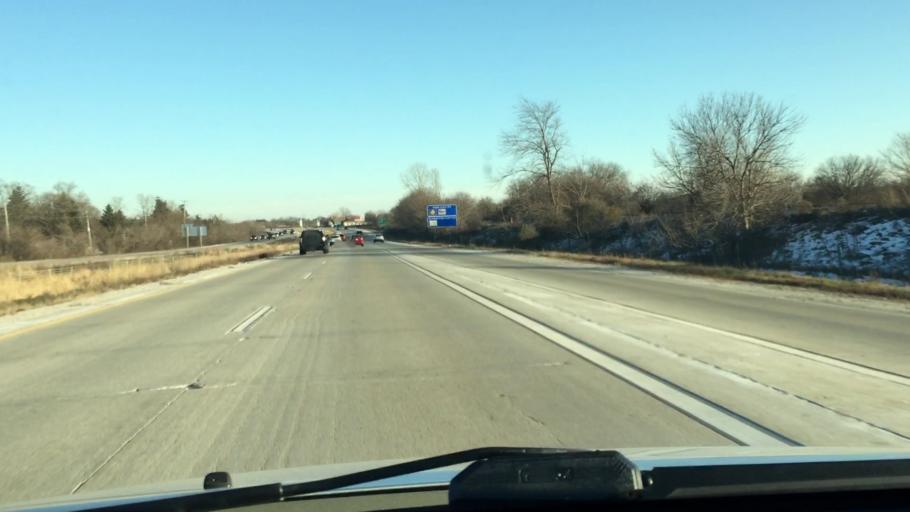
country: US
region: Wisconsin
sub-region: Waukesha County
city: Okauchee Lake
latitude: 43.1057
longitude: -88.4273
